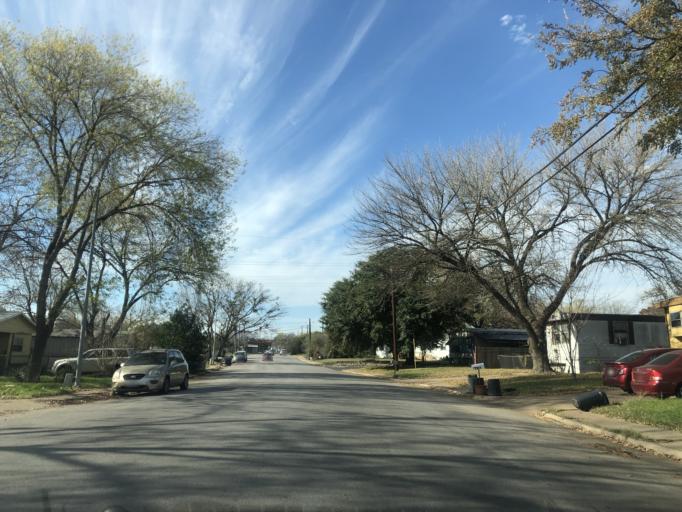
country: US
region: Texas
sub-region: Travis County
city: Onion Creek
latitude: 30.1828
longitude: -97.7666
